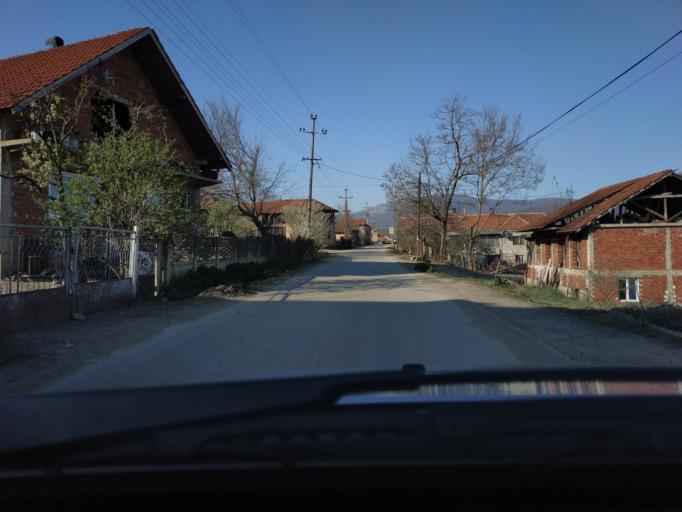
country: RS
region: Central Serbia
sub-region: Nisavski Okrug
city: Aleksinac
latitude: 43.5086
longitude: 21.7971
